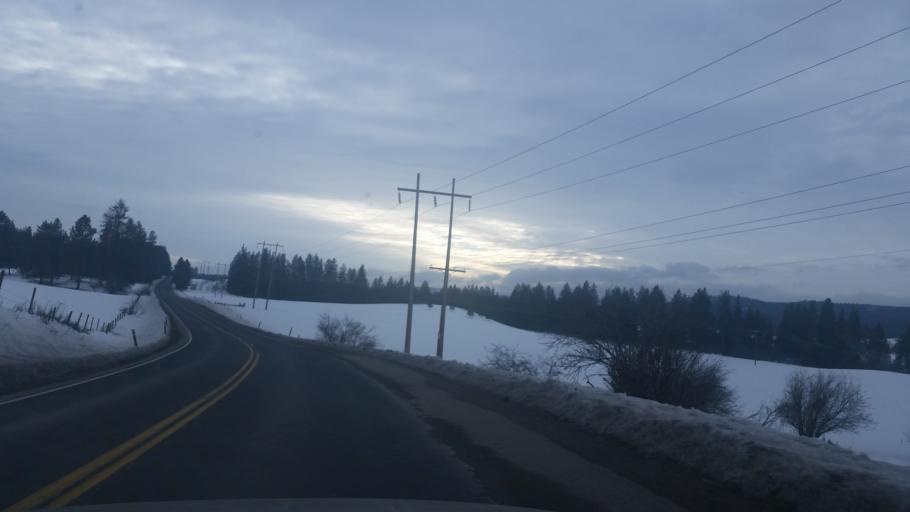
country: US
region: Washington
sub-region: Stevens County
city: Chewelah
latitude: 48.1048
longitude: -117.7577
